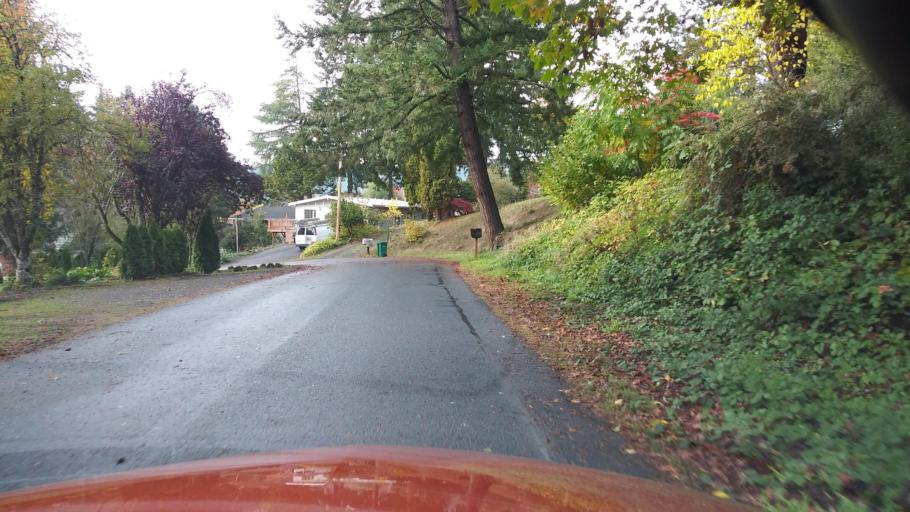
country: US
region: Oregon
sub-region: Washington County
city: Forest Grove
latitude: 45.5331
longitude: -123.1374
